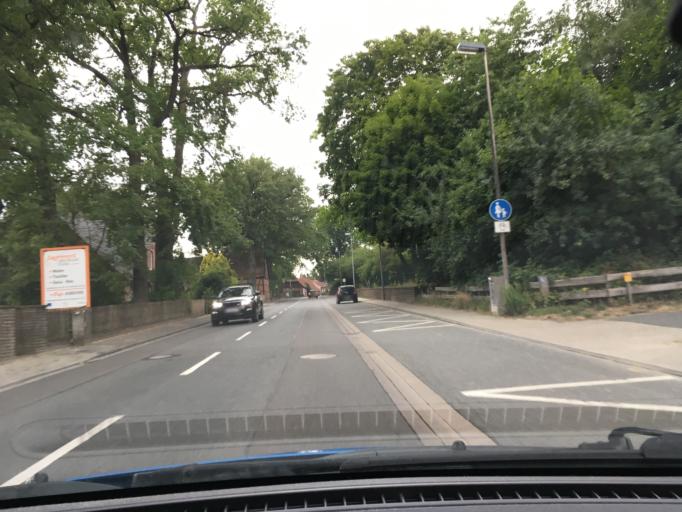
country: DE
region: Lower Saxony
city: Celle
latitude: 52.6329
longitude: 10.1148
